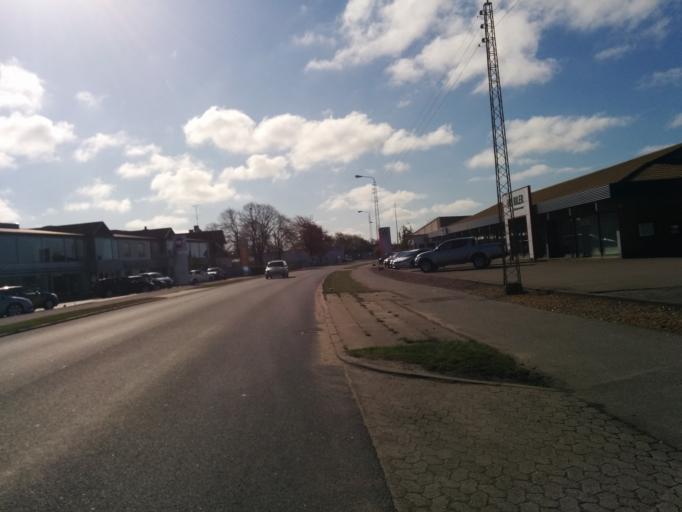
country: DK
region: Central Jutland
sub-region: Viborg Kommune
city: Viborg
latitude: 56.4656
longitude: 9.4011
